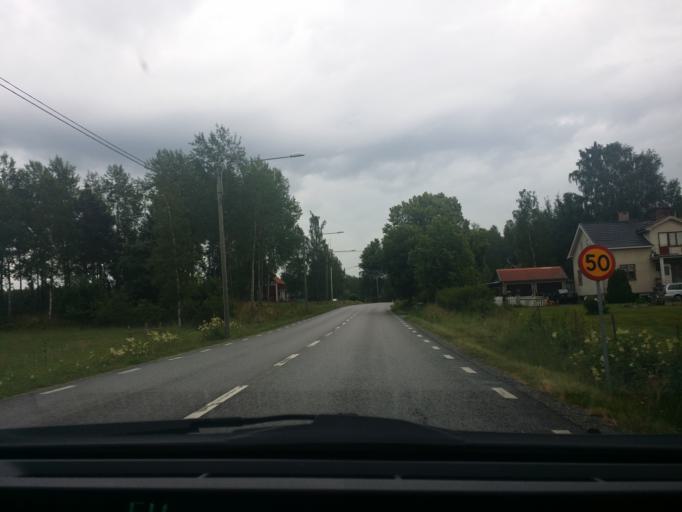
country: SE
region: OErebro
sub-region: Orebro Kommun
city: Hovsta
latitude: 59.4405
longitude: 15.2508
